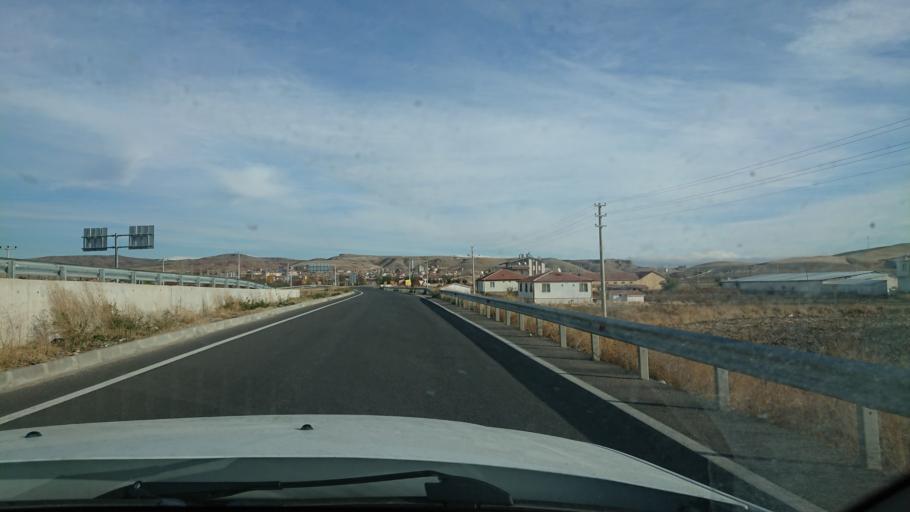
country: TR
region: Aksaray
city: Acipinar
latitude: 38.4774
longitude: 33.9002
